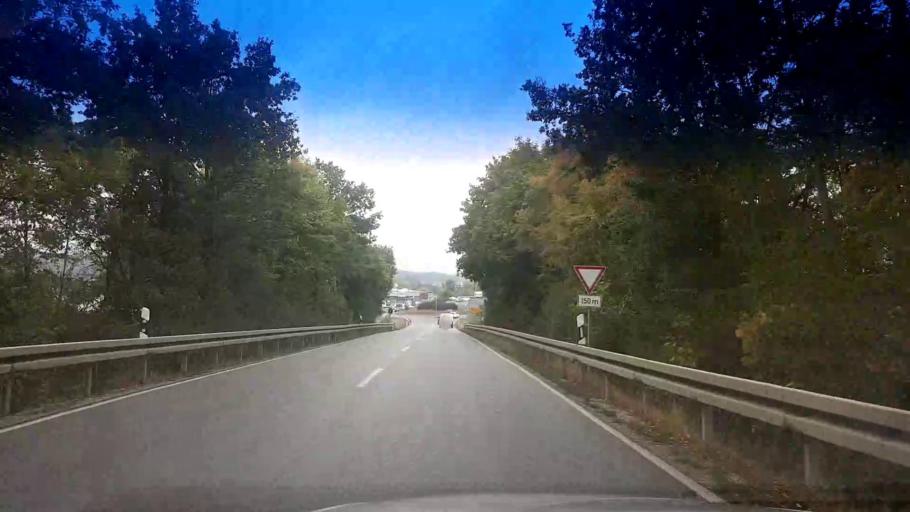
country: DE
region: Bavaria
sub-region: Upper Franconia
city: Eggolsheim
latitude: 49.7715
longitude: 11.0385
